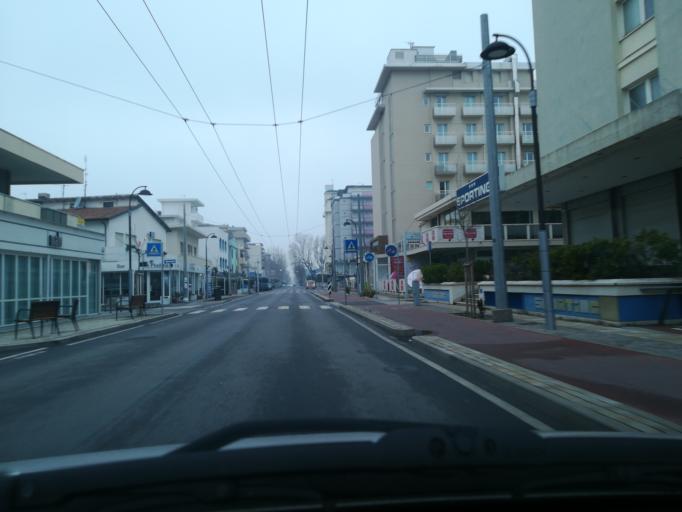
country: IT
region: Emilia-Romagna
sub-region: Provincia di Rimini
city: Riccione
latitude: 44.0142
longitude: 12.6445
